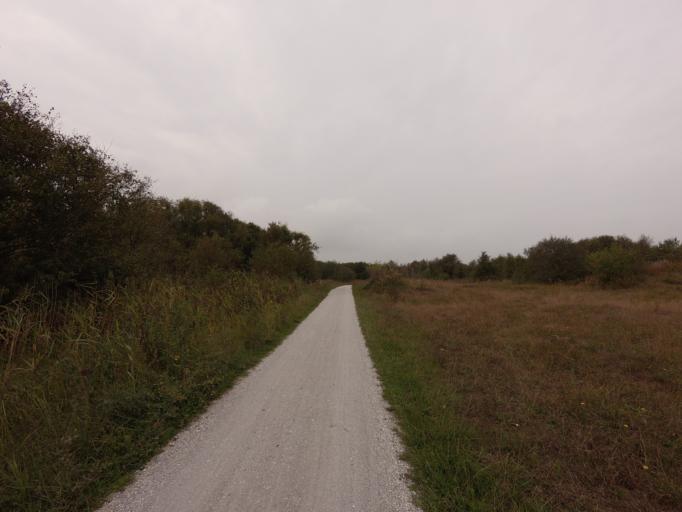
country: NL
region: Friesland
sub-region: Gemeente Schiermonnikoog
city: Schiermonnikoog
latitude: 53.4913
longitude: 6.1991
